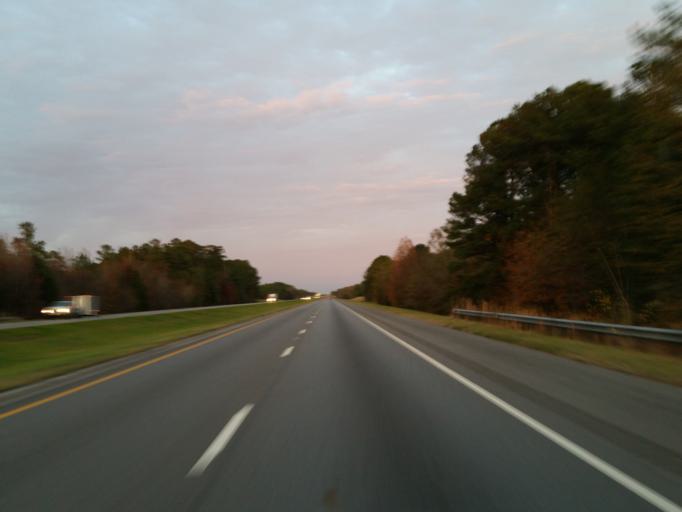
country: US
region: Alabama
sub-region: Sumter County
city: Livingston
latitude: 32.7232
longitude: -88.1163
